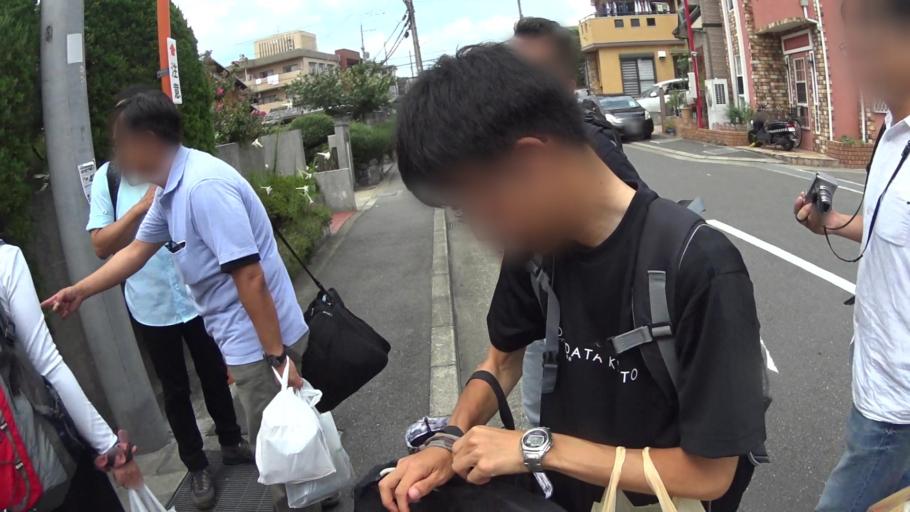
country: JP
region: Kyoto
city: Yawata
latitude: 34.9123
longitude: 135.6974
